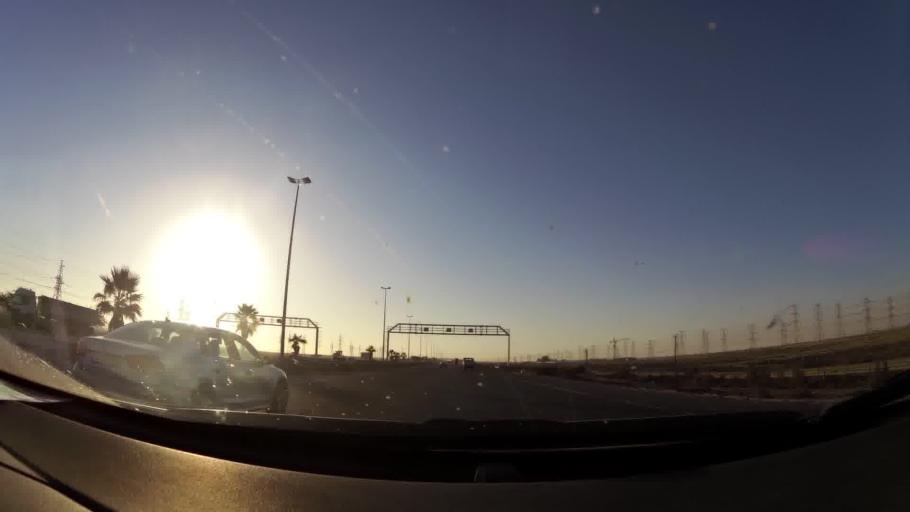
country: KW
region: Al Ahmadi
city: Al Fahahil
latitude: 28.8969
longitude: 48.2205
